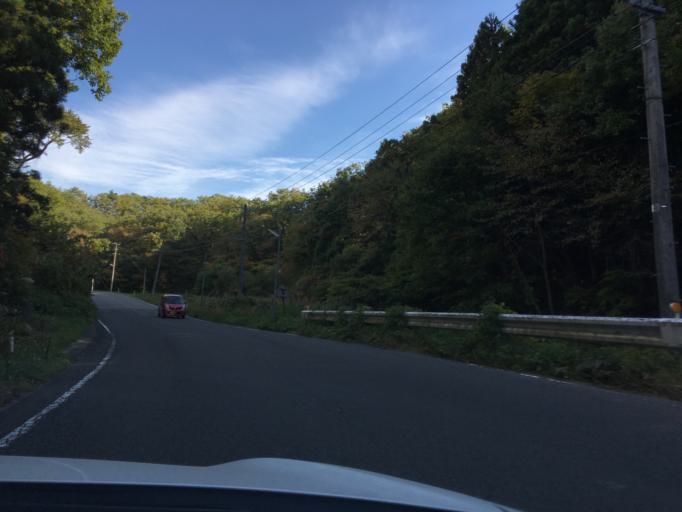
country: JP
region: Fukushima
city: Miharu
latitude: 37.3589
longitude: 140.5327
